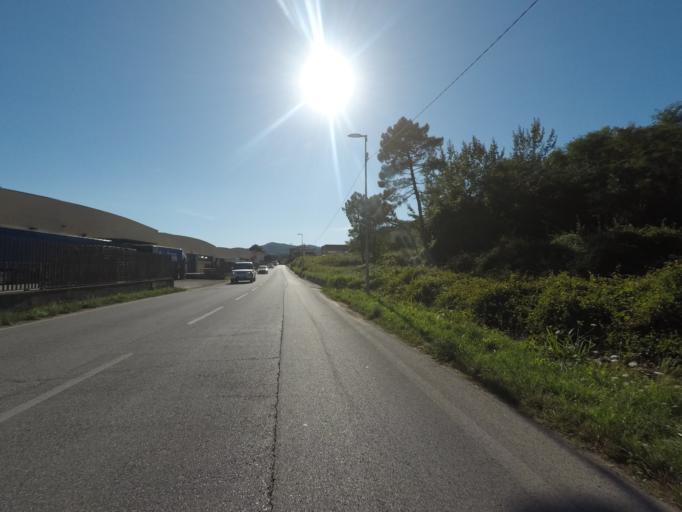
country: IT
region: Tuscany
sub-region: Provincia di Lucca
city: San Martino in Freddana-Monsagrati
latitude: 43.9085
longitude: 10.4246
